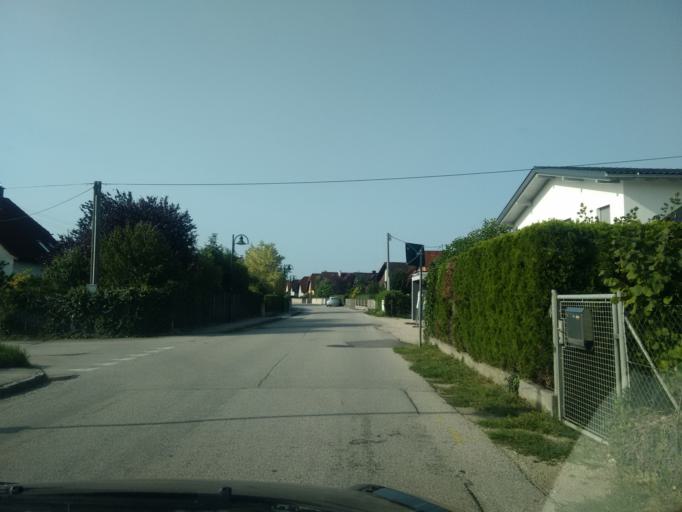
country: AT
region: Upper Austria
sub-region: Wels-Land
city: Gunskirchen
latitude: 48.1262
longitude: 13.9428
